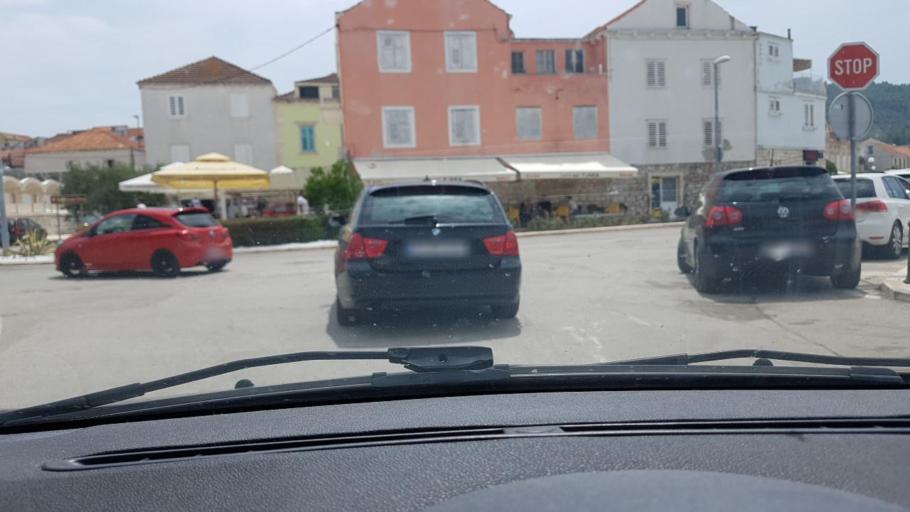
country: HR
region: Dubrovacko-Neretvanska
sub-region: Grad Dubrovnik
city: Vela Luka
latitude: 42.9616
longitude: 16.7147
